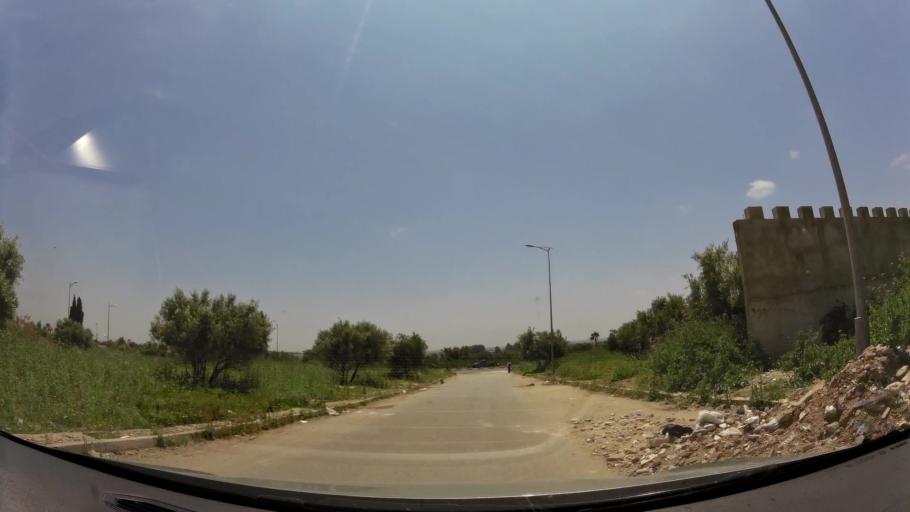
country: MA
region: Fes-Boulemane
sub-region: Fes
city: Fes
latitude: 34.0487
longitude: -5.0437
